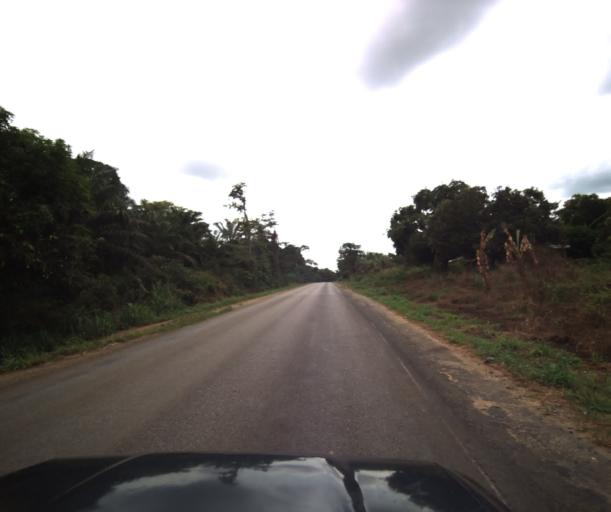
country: CM
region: Centre
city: Eseka
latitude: 3.8495
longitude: 10.4860
